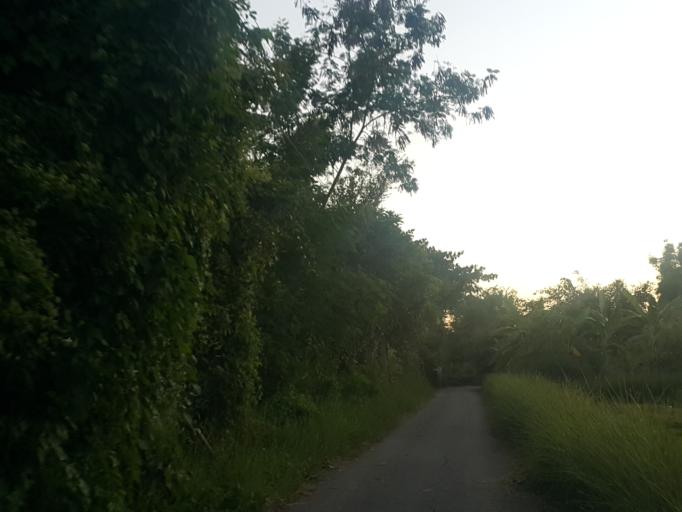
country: TH
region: Chiang Mai
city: San Kamphaeng
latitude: 18.8254
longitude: 99.1444
